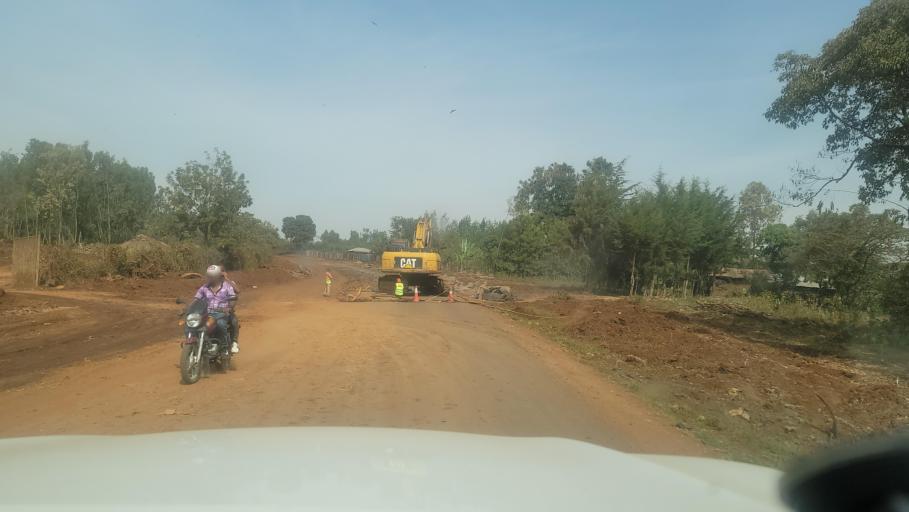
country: ET
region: Oromiya
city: Jima
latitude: 7.7222
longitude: 36.8052
